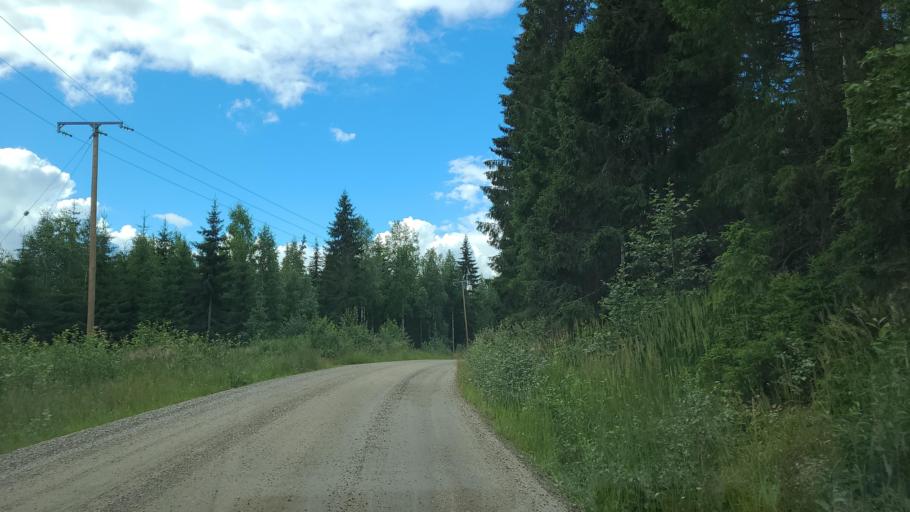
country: FI
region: Northern Savo
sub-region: Koillis-Savo
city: Kaavi
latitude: 62.9898
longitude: 28.5305
